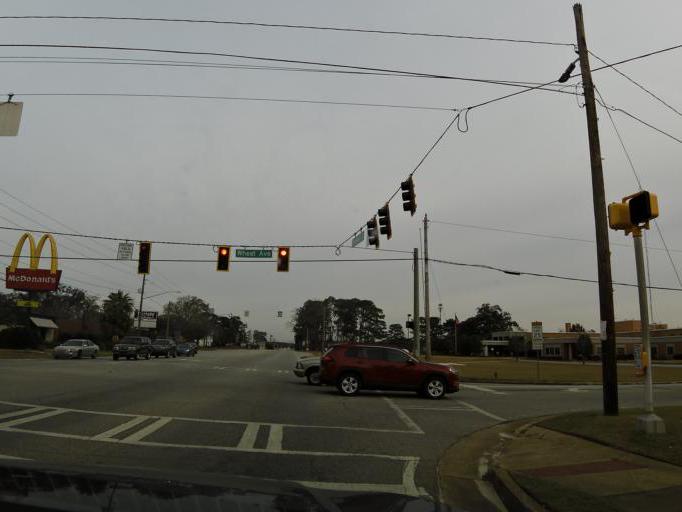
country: US
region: Georgia
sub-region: Decatur County
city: Bainbridge
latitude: 30.9038
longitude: -84.5539
